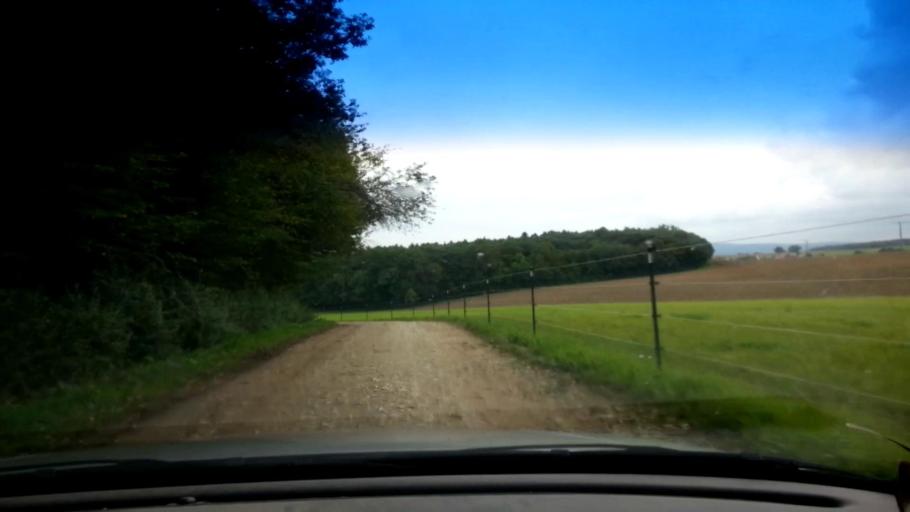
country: DE
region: Bavaria
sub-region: Upper Franconia
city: Litzendorf
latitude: 49.9315
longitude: 11.0046
